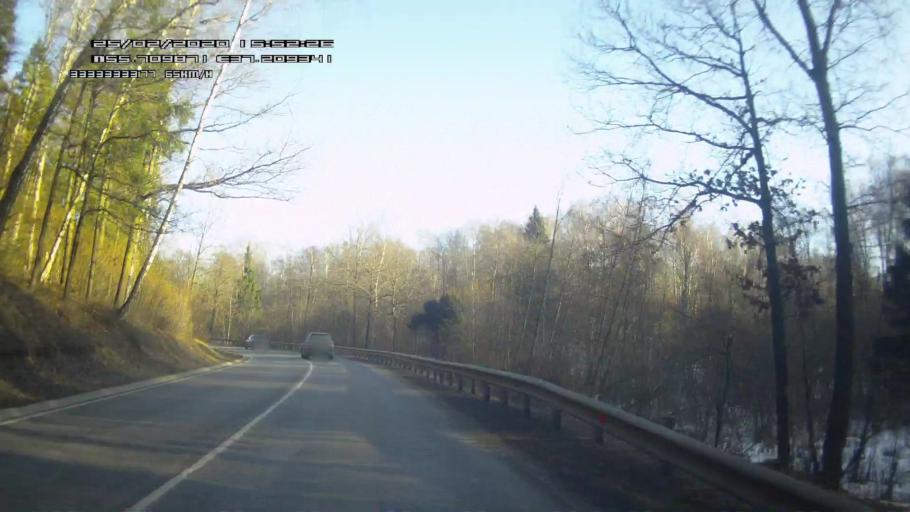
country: RU
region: Moskovskaya
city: Gorki Vtoryye
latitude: 55.7099
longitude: 37.2093
